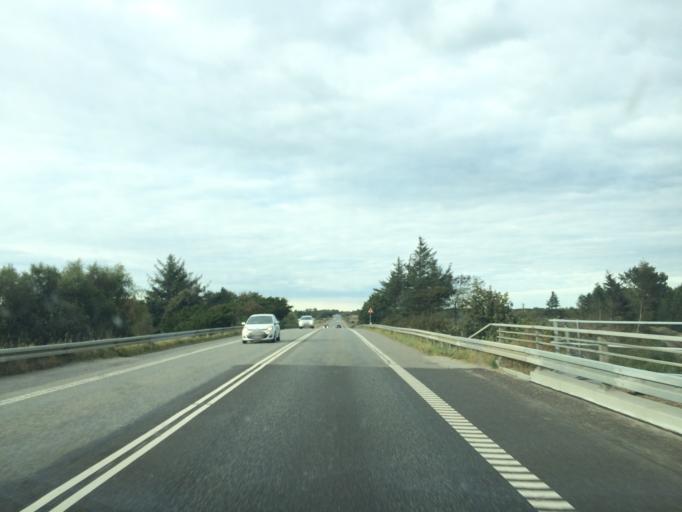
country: DK
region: Central Jutland
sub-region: Ringkobing-Skjern Kommune
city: Ringkobing
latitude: 56.1276
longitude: 8.2802
